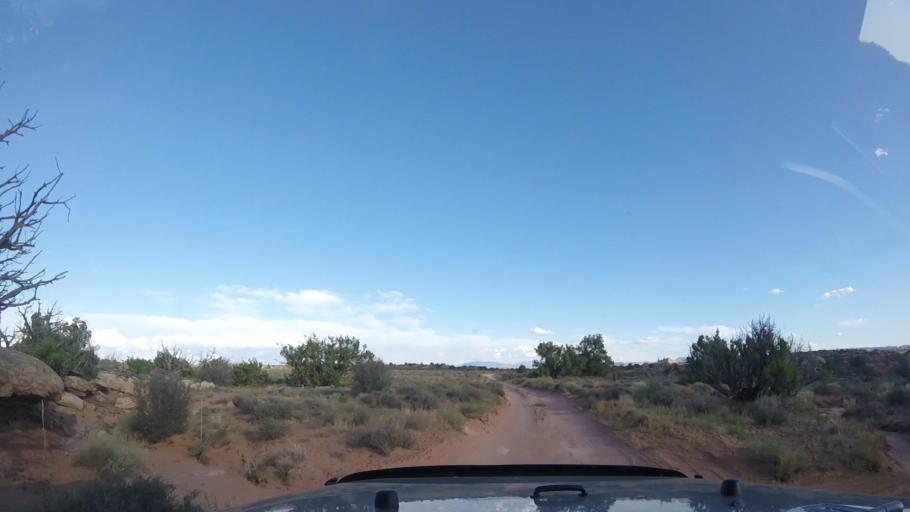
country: US
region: Utah
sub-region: Grand County
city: Moab
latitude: 38.2052
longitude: -109.7855
